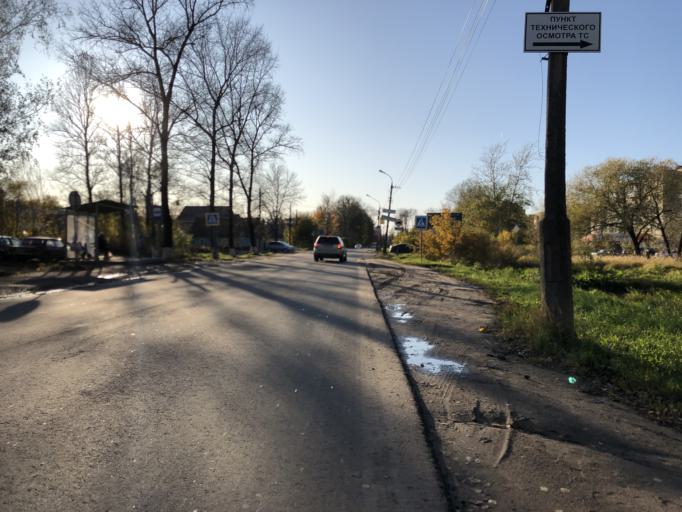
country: RU
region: Tverskaya
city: Rzhev
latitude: 56.2465
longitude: 34.3359
